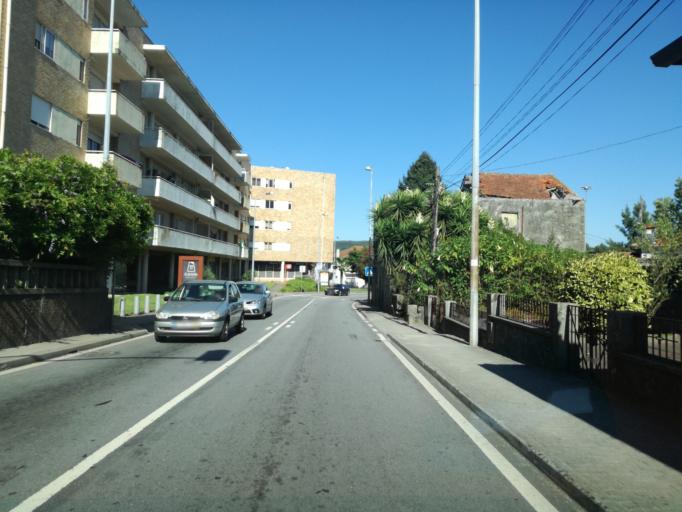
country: PT
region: Porto
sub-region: Trofa
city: Sao Romao do Coronado
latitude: 41.2793
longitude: -8.5544
